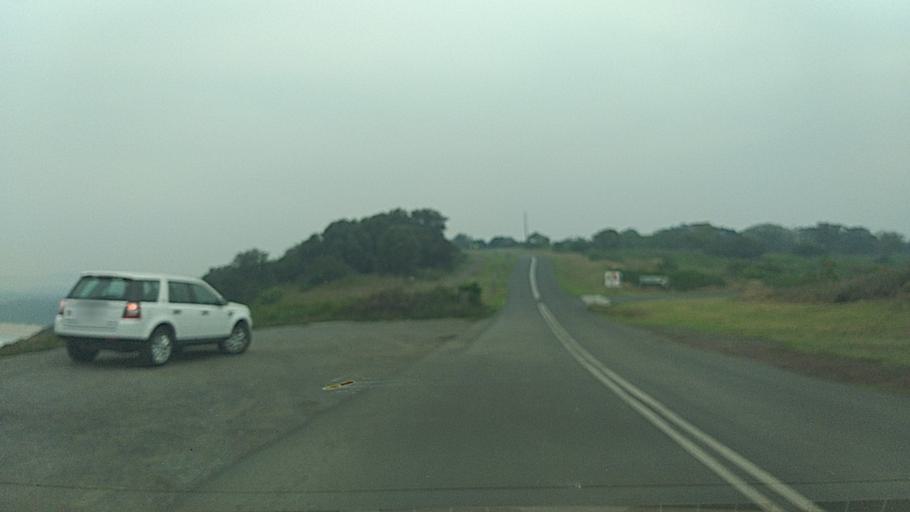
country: AU
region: New South Wales
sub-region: Shellharbour
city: Croom
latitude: -34.6113
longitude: 150.8579
